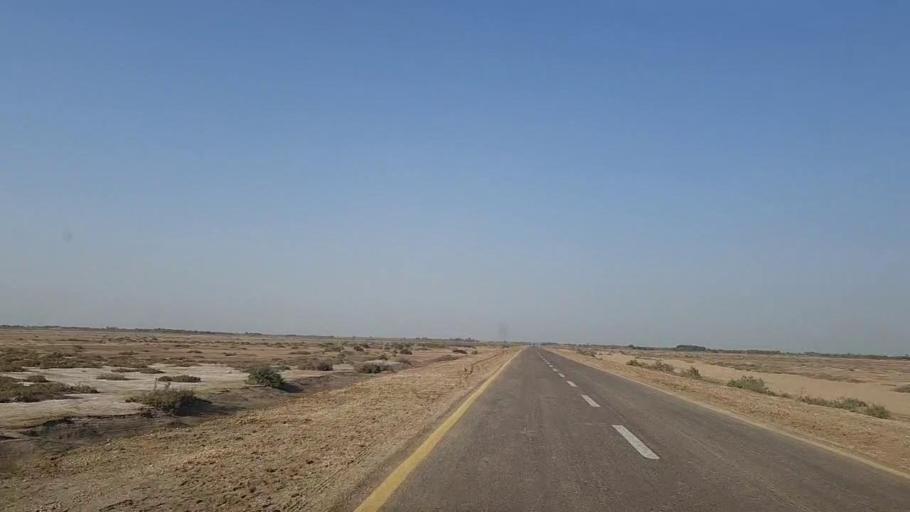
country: PK
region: Sindh
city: Jati
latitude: 24.4980
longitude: 68.3768
